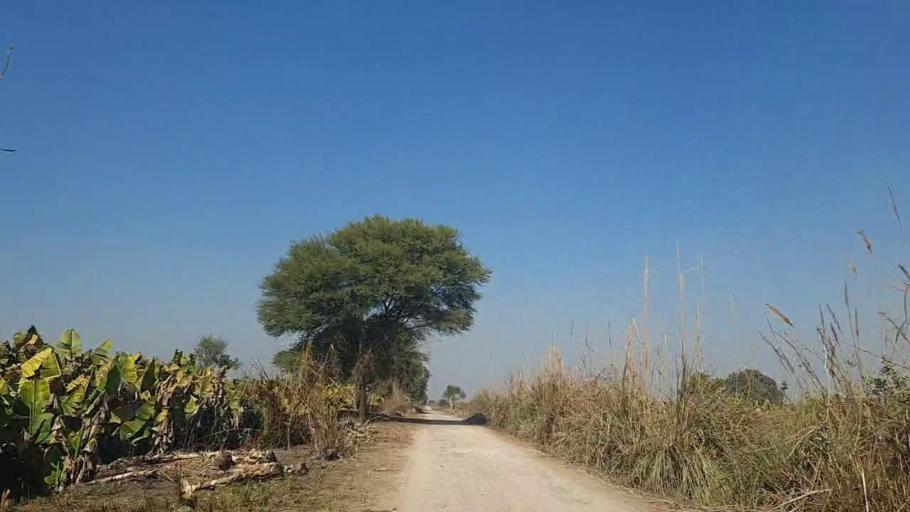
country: PK
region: Sindh
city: Sakrand
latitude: 26.2616
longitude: 68.2209
